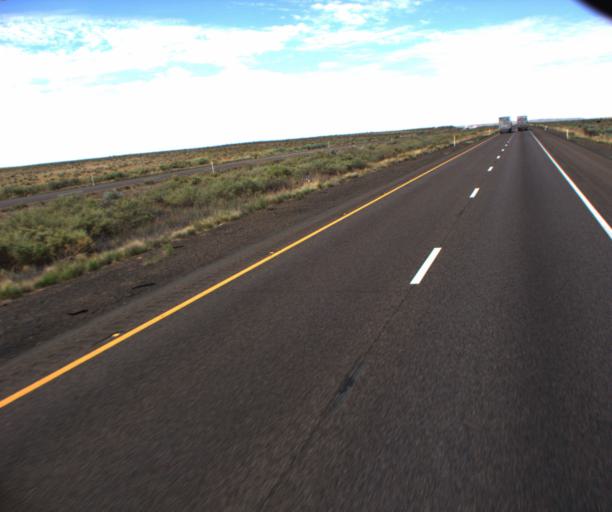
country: US
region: Arizona
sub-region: Apache County
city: Houck
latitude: 35.0964
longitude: -109.6631
